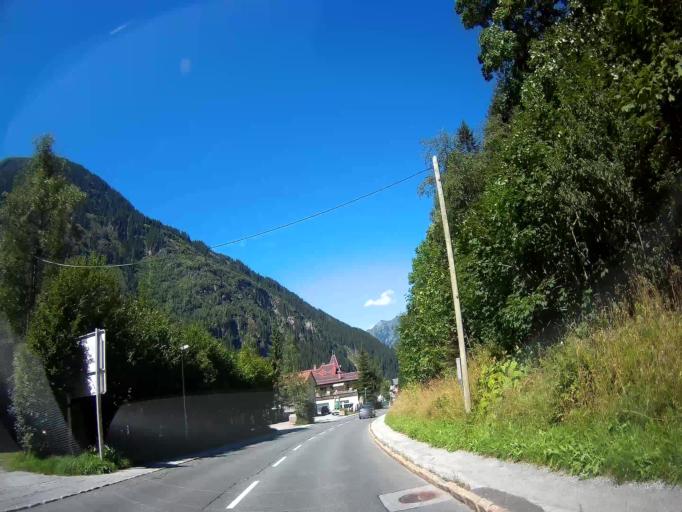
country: AT
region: Salzburg
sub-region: Politischer Bezirk Sankt Johann im Pongau
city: Bad Gastein
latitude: 47.0889
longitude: 13.1202
